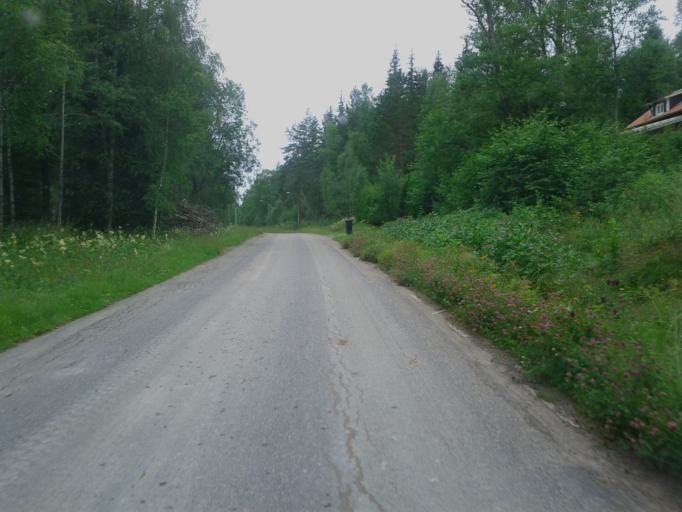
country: SE
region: Dalarna
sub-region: Borlange Kommun
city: Borlaenge
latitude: 60.3415
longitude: 15.4179
